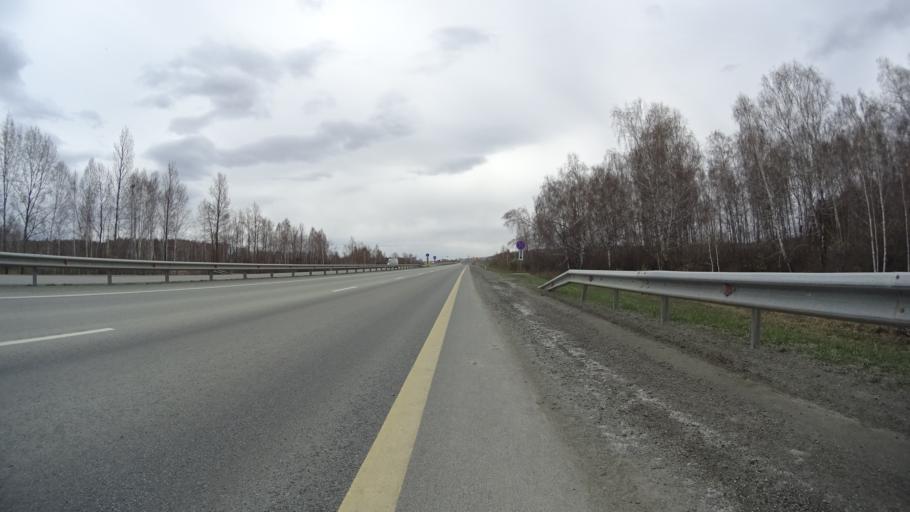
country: RU
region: Chelyabinsk
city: Yemanzhelinka
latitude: 54.8276
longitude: 61.3106
